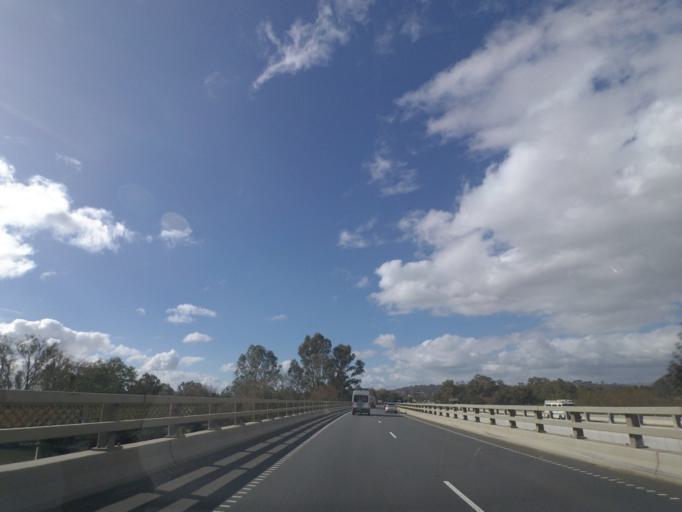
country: AU
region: New South Wales
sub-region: Albury Municipality
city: South Albury
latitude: -36.1004
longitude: 146.9092
